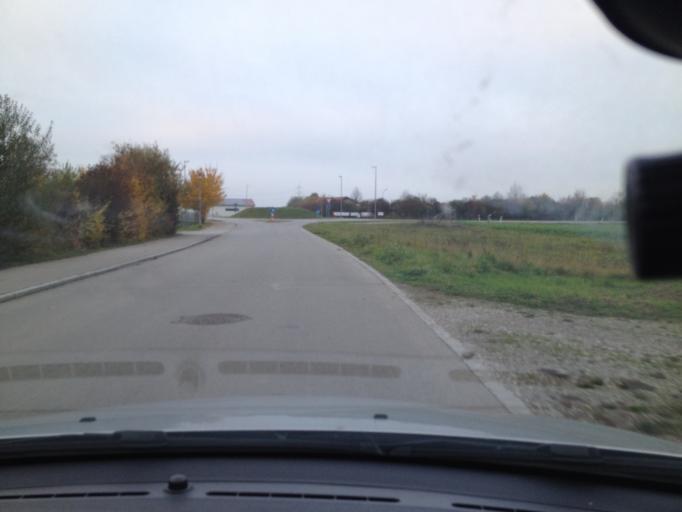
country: DE
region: Bavaria
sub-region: Swabia
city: Oberottmarshausen
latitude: 48.2209
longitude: 10.8480
